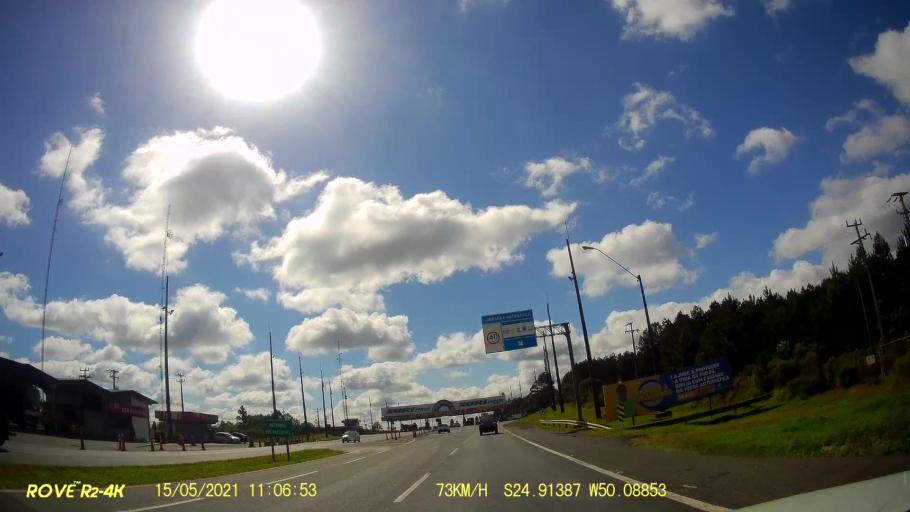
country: BR
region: Parana
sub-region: Carambei
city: Carambei
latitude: -24.9140
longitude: -50.0887
